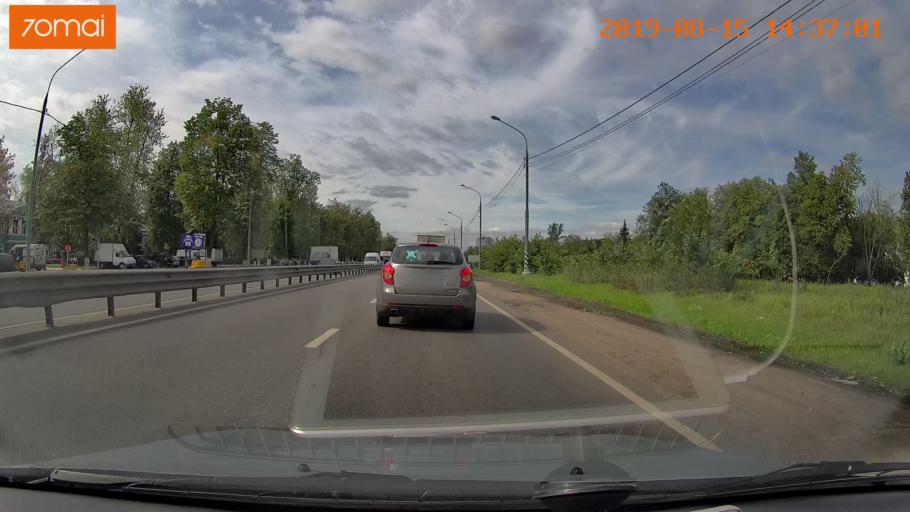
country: RU
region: Moskovskaya
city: Tomilino
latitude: 55.6504
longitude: 37.9304
